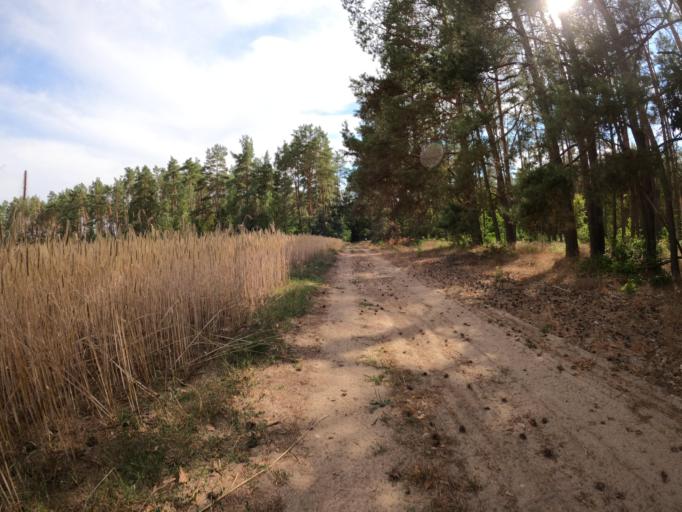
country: DE
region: Brandenburg
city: Lychen
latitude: 53.2701
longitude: 13.4377
